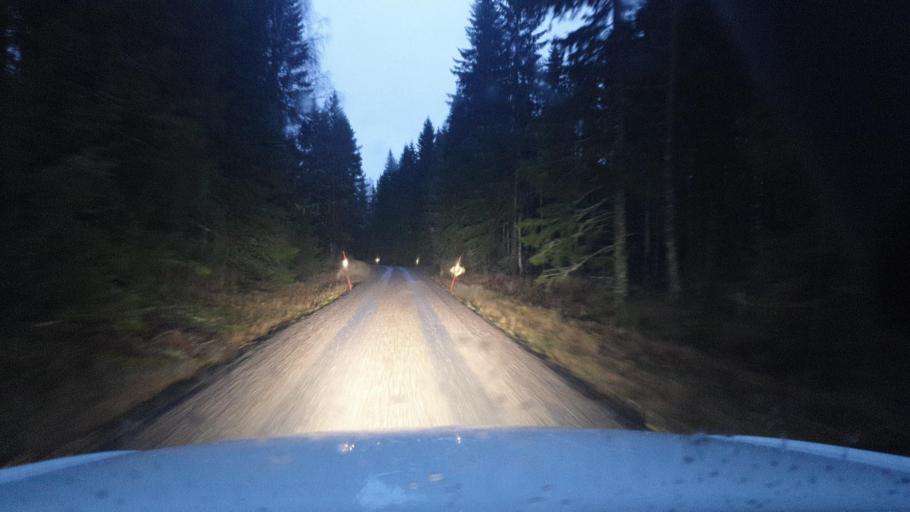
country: SE
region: Vaermland
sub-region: Eda Kommun
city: Charlottenberg
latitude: 60.0328
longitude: 12.6316
